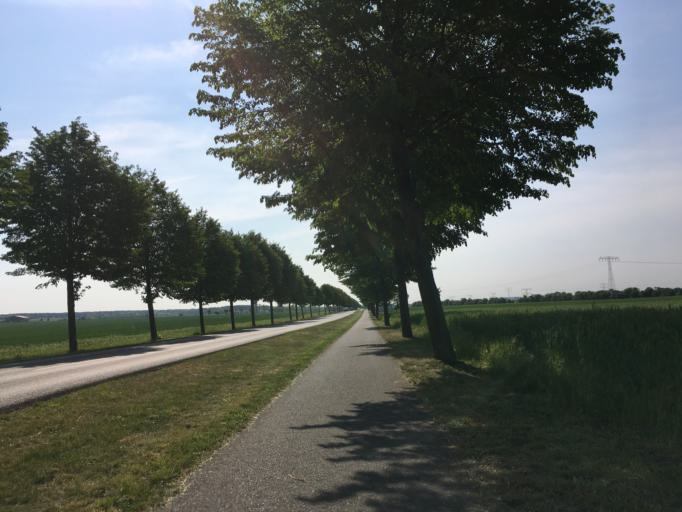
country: DE
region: Berlin
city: Falkenberg
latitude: 52.5980
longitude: 13.5382
